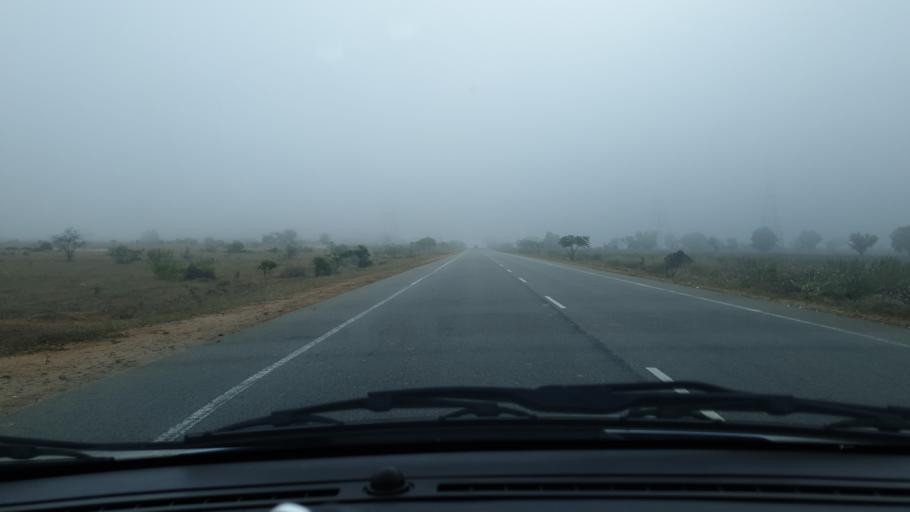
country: IN
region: Telangana
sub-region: Nalgonda
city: Devarkonda
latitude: 16.6297
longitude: 78.6618
